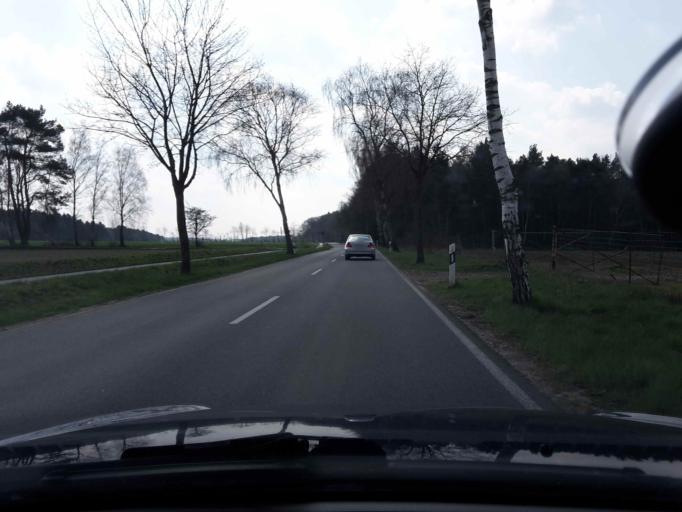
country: DE
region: Lower Saxony
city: Buchholz in der Nordheide
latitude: 53.3074
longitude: 9.9075
